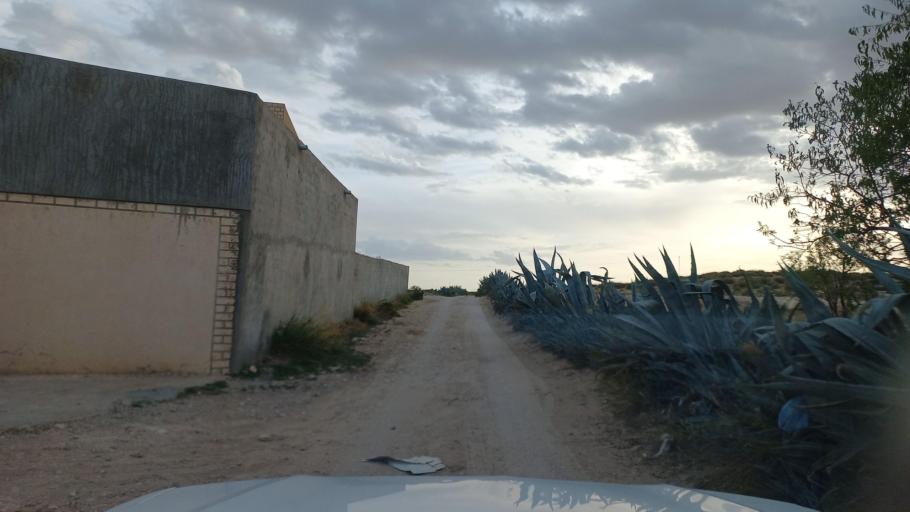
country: TN
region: Al Qasrayn
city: Sbiba
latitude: 35.4263
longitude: 9.0957
